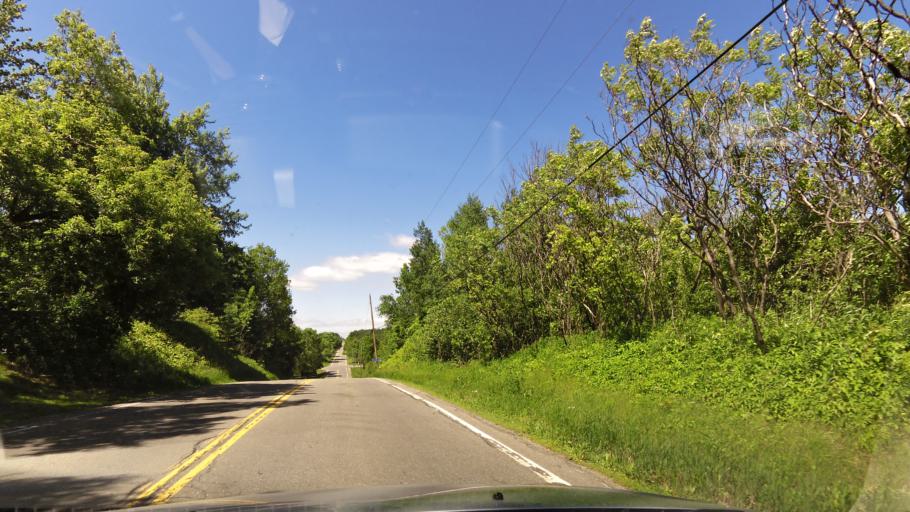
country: CA
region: Ontario
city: Newmarket
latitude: 43.9628
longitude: -79.5377
